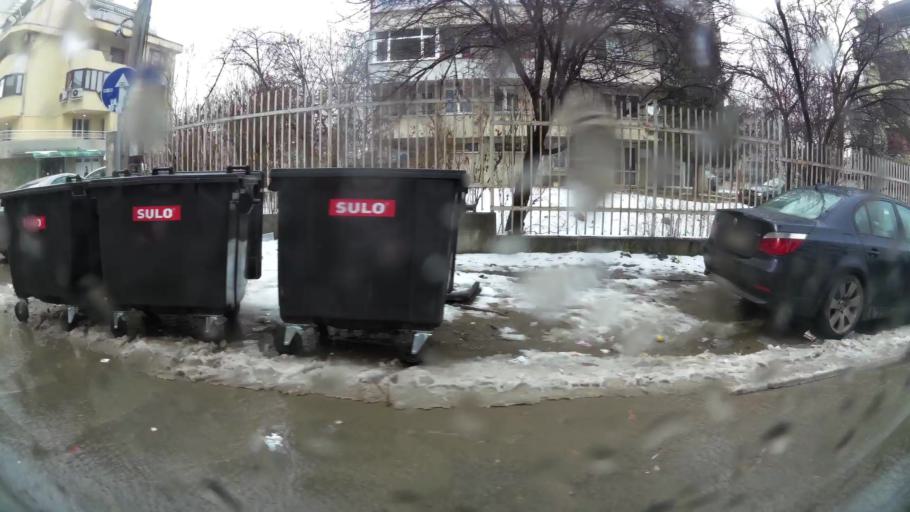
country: BG
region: Sofia-Capital
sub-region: Stolichna Obshtina
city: Sofia
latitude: 42.6609
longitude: 23.2827
